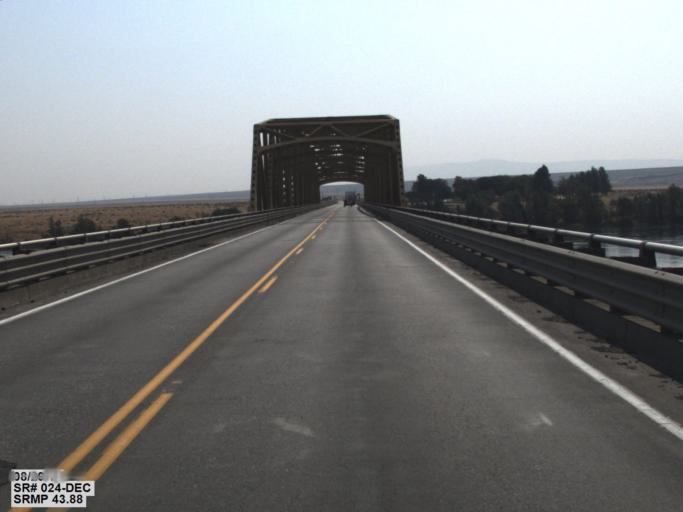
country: US
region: Washington
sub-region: Grant County
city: Desert Aire
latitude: 46.6433
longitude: -119.7334
